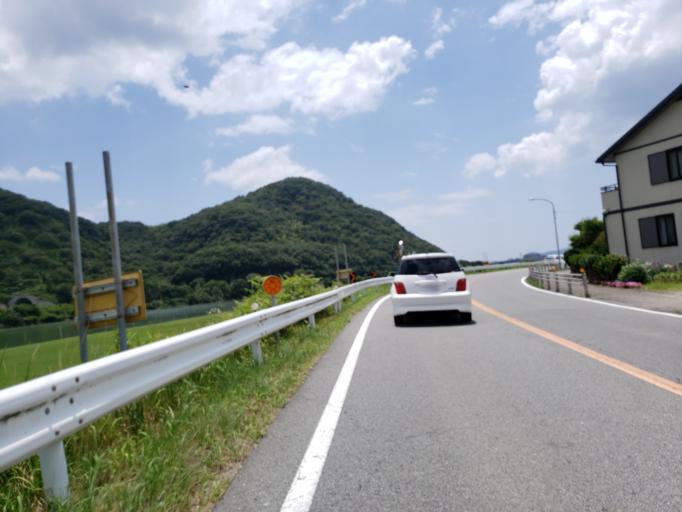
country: JP
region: Hyogo
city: Kariya
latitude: 34.7577
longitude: 134.4107
